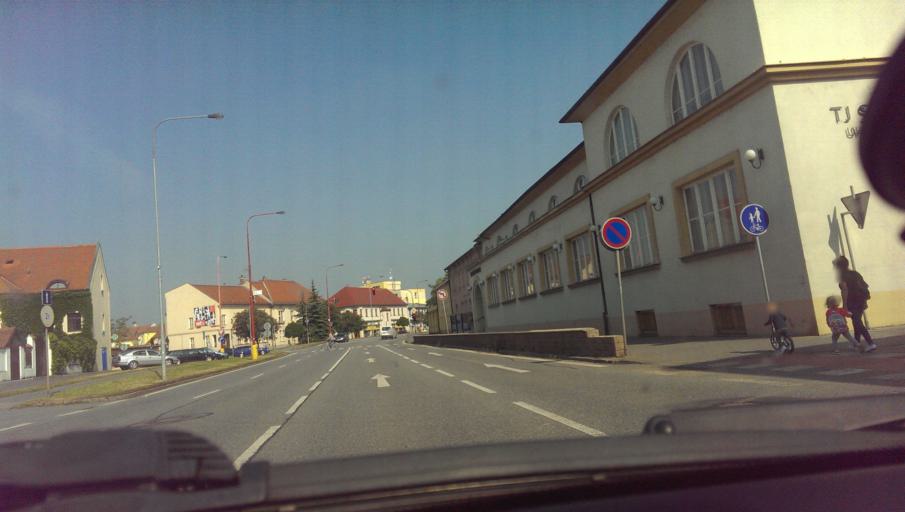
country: CZ
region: Zlin
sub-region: Okres Uherske Hradiste
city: Uherske Hradiste
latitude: 49.0712
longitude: 17.4607
